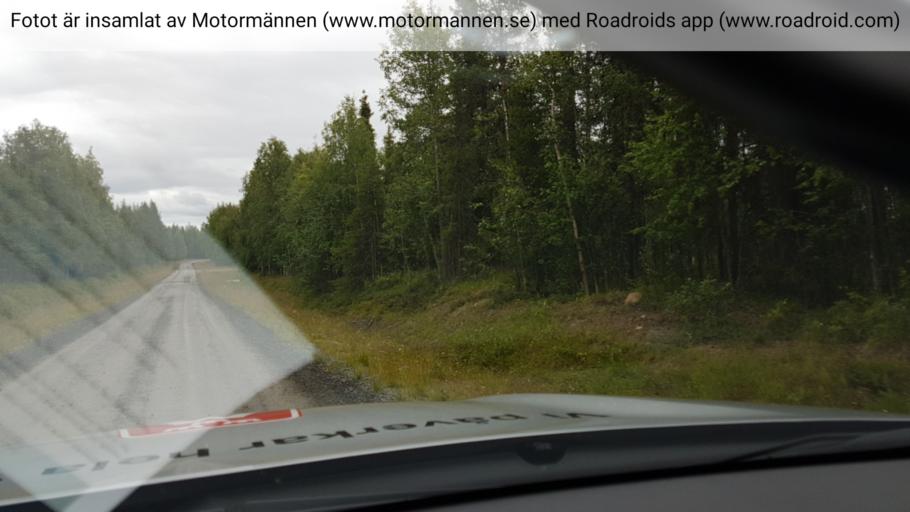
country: SE
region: Norrbotten
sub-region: Pajala Kommun
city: Pajala
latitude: 67.0053
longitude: 22.8546
